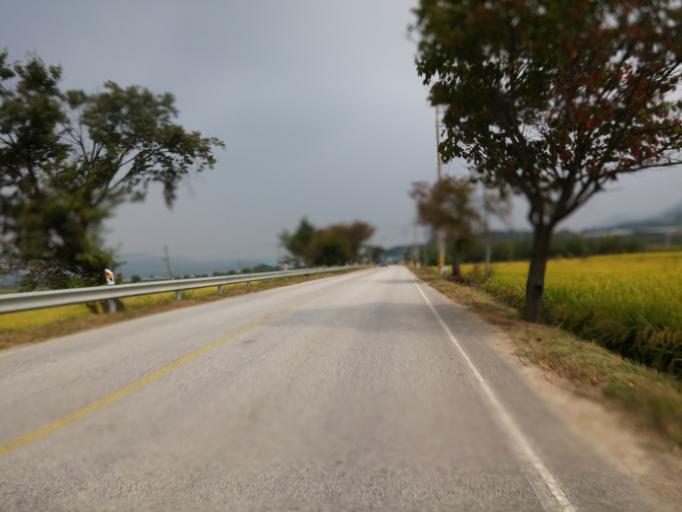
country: KR
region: Chungcheongbuk-do
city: Okcheon
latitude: 36.4026
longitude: 127.7452
